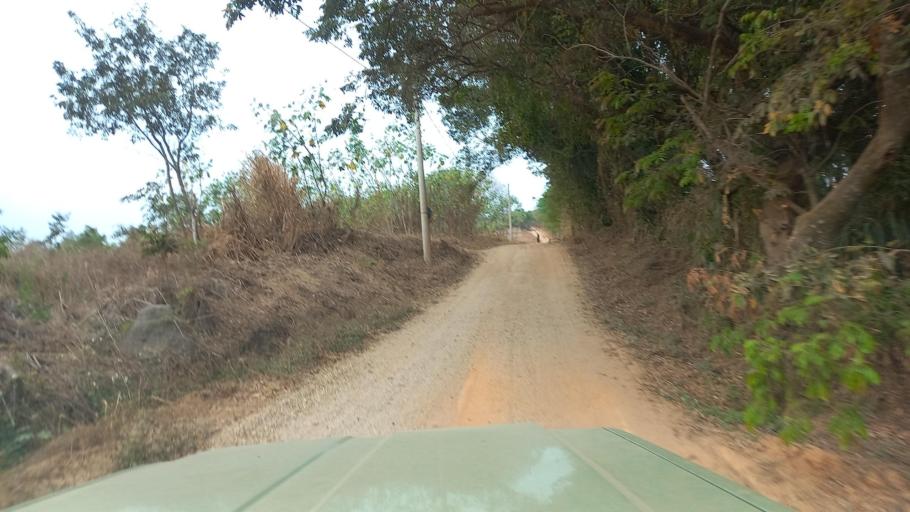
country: BR
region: Sao Paulo
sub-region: Moji-Guacu
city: Mogi-Gaucu
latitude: -22.2837
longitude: -46.8449
